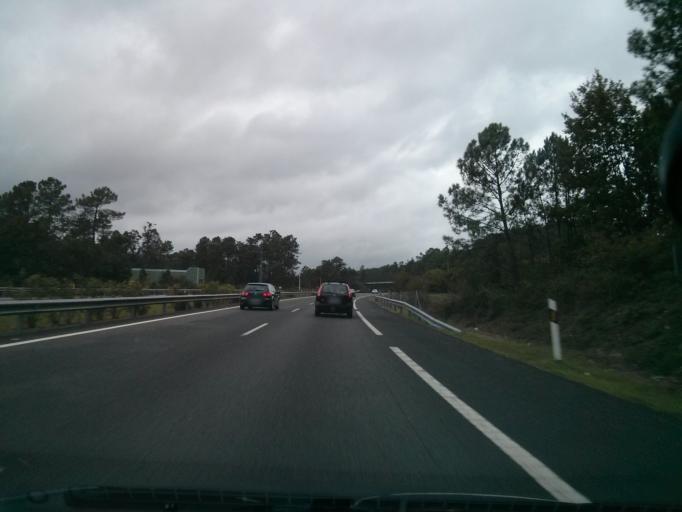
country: ES
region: Galicia
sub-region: Provincia de Pontevedra
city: Ponteareas
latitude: 42.1564
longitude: -8.5203
